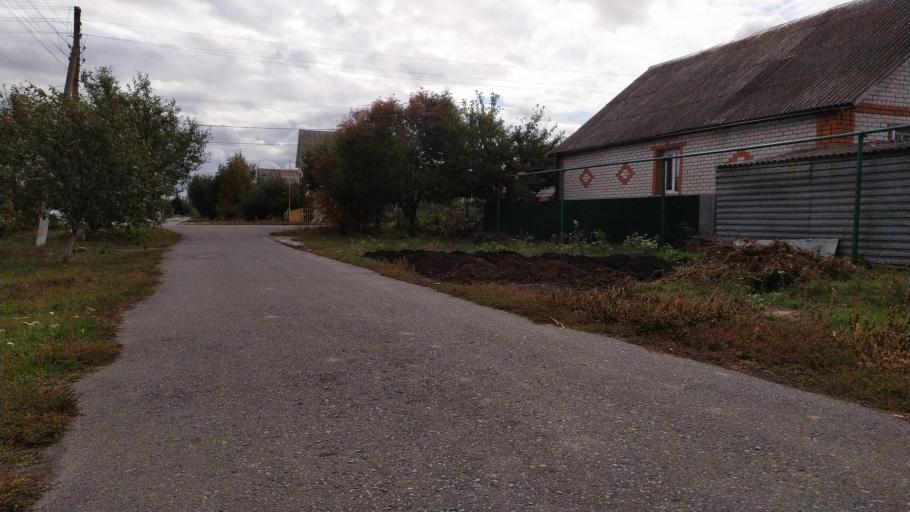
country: RU
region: Kursk
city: Kursk
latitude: 51.6444
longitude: 36.1533
